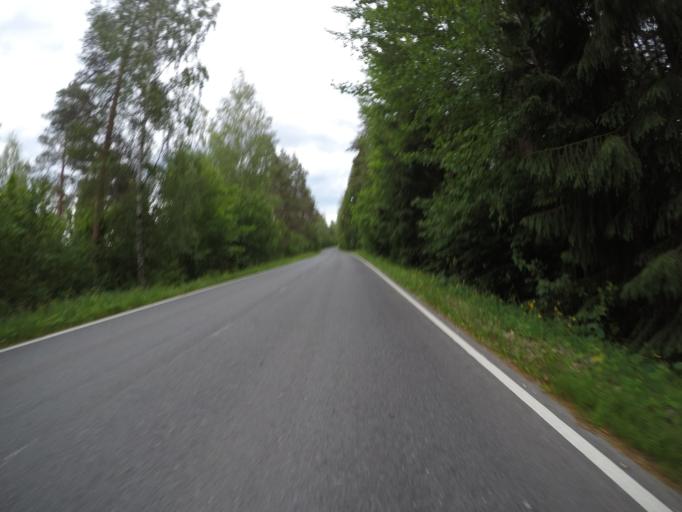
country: FI
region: Haeme
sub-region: Haemeenlinna
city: Haemeenlinna
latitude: 60.9748
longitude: 24.4640
